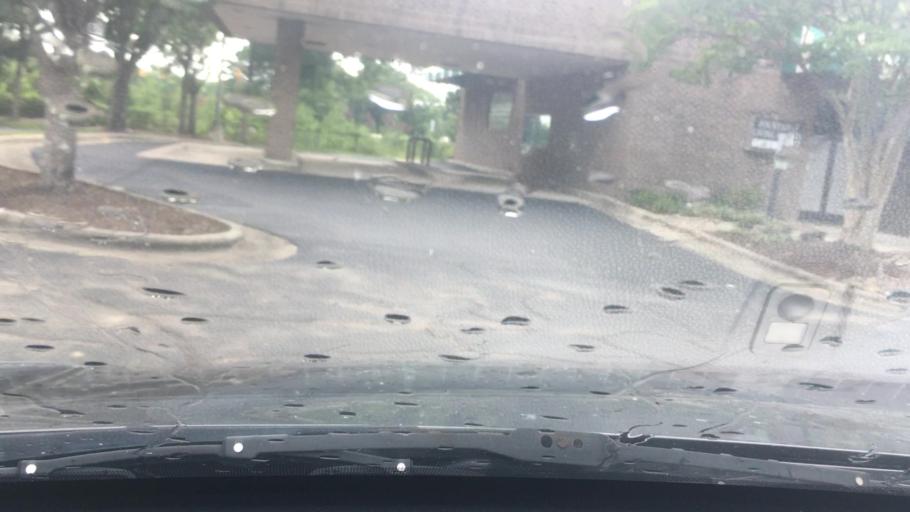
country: US
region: North Carolina
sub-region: Wake County
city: Raleigh
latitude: 35.7966
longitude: -78.5813
